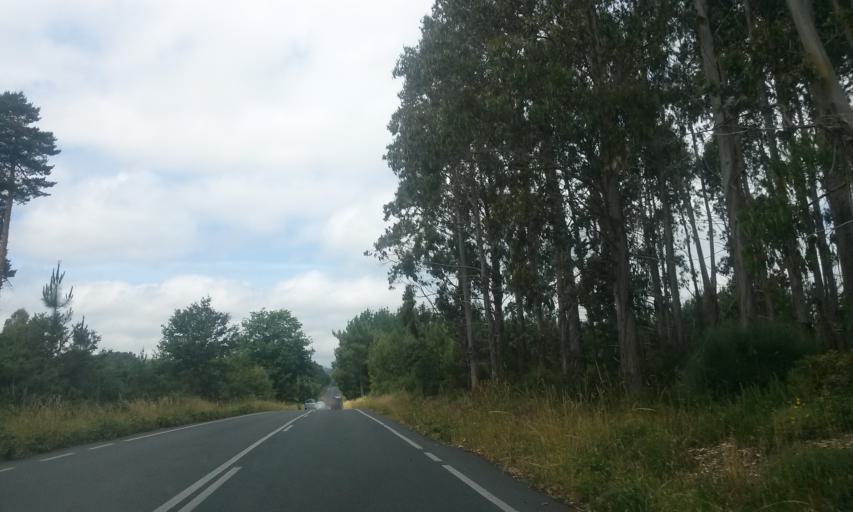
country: ES
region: Galicia
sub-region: Provincia de Lugo
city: Friol
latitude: 43.0362
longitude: -7.8074
